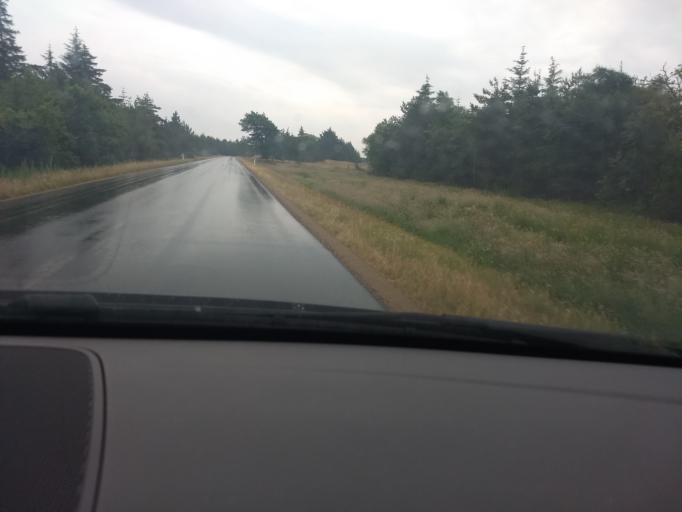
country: DK
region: South Denmark
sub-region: Fano Kommune
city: Nordby
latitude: 55.3968
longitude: 8.4229
